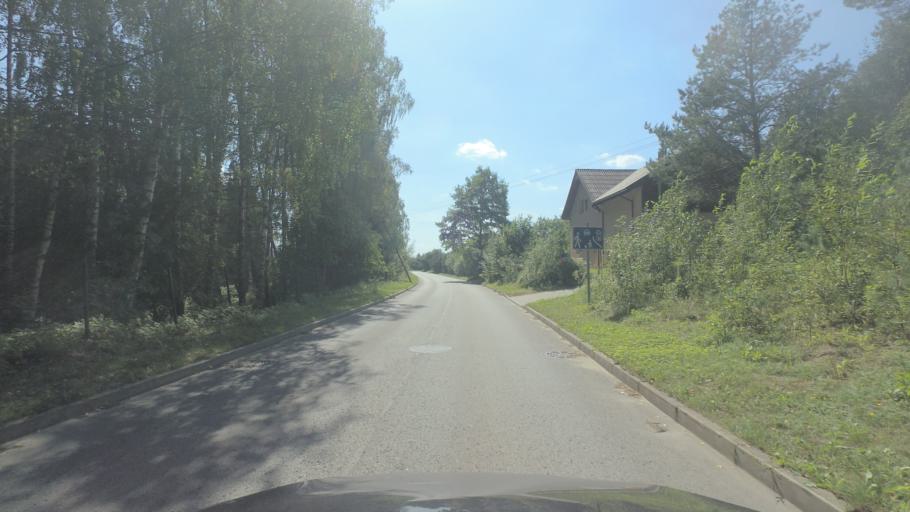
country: LT
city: Nemencine
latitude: 54.8433
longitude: 25.3718
